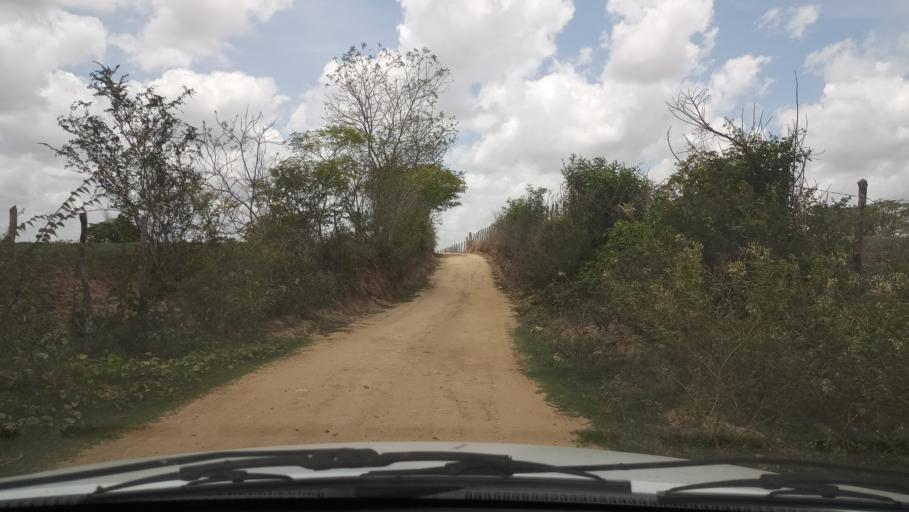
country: BR
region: Rio Grande do Norte
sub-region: Brejinho
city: Brejinho
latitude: -6.2740
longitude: -35.3357
